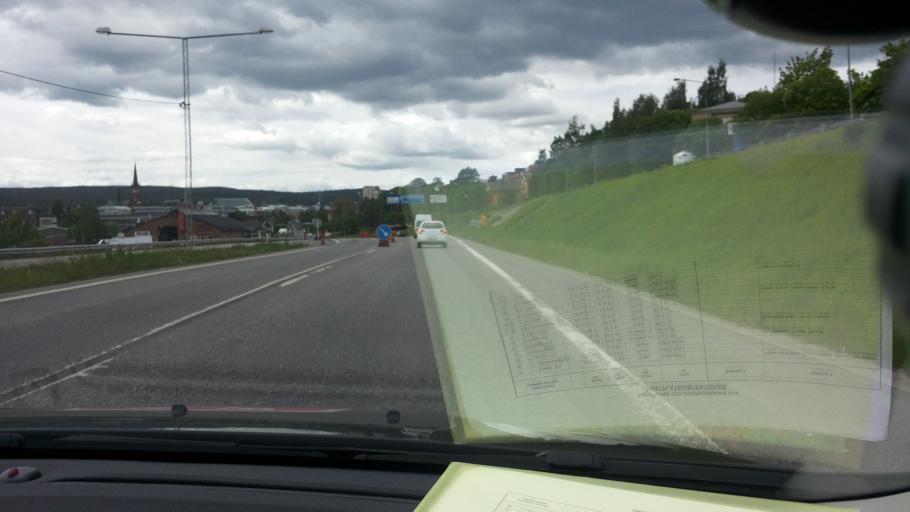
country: SE
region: Vaesternorrland
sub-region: Sundsvalls Kommun
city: Sundsvall
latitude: 62.3951
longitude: 17.3203
